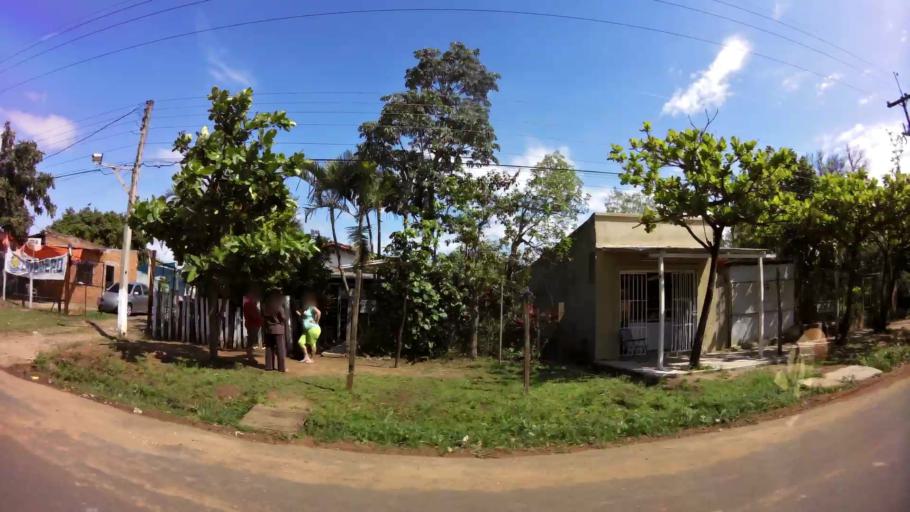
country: PY
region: Central
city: Limpio
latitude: -25.2519
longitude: -57.4922
